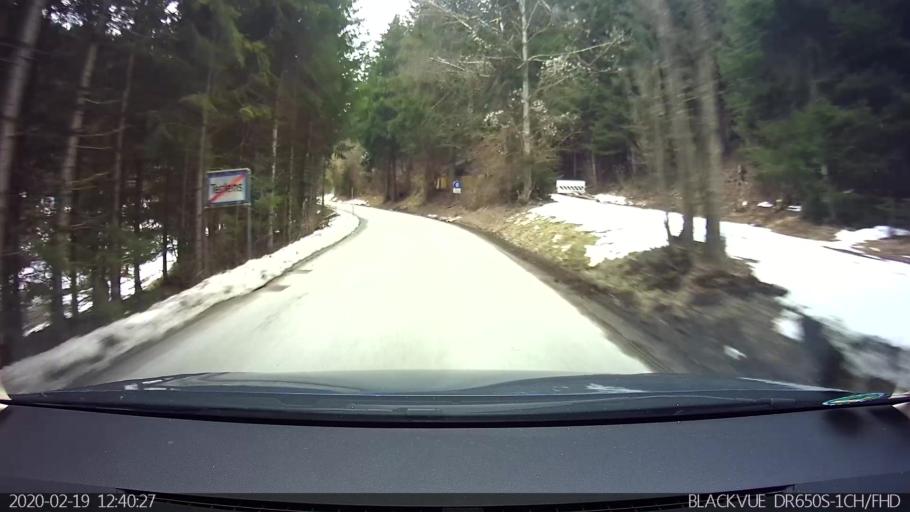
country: AT
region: Tyrol
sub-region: Politischer Bezirk Schwaz
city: Terfens
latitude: 47.3255
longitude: 11.6360
